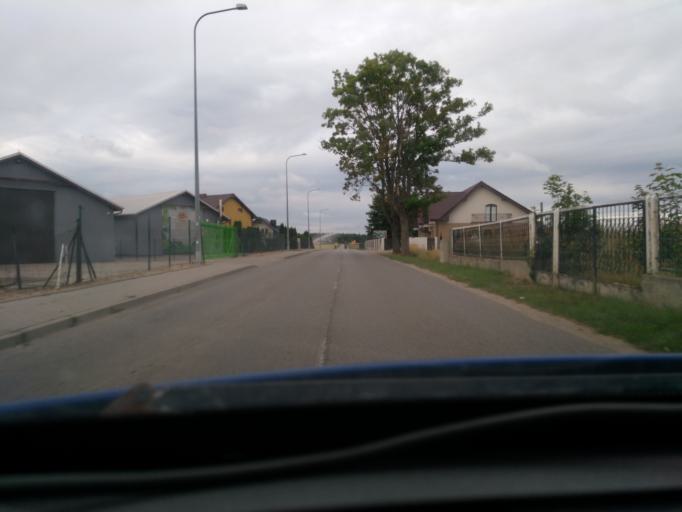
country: PL
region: Pomeranian Voivodeship
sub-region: Powiat kartuski
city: Banino
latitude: 54.3854
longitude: 18.4058
